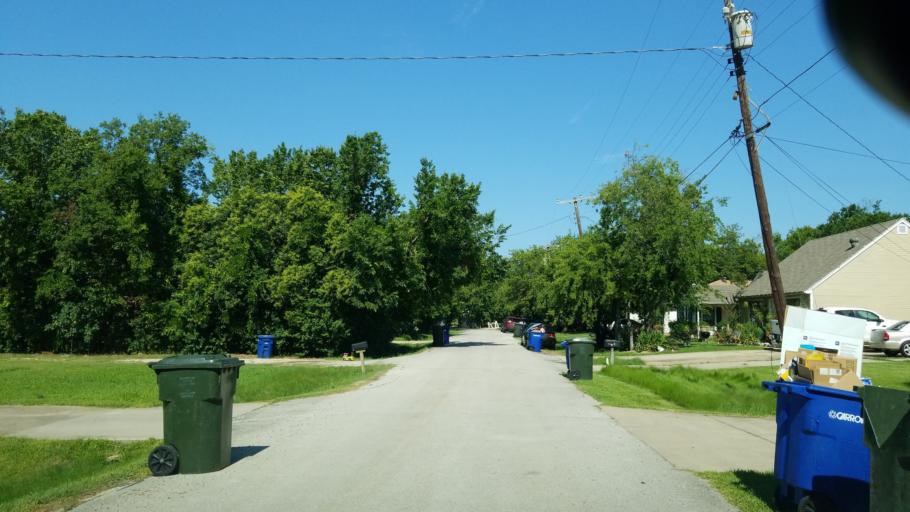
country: US
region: Texas
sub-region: Dallas County
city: Carrollton
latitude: 32.9564
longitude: -96.9039
